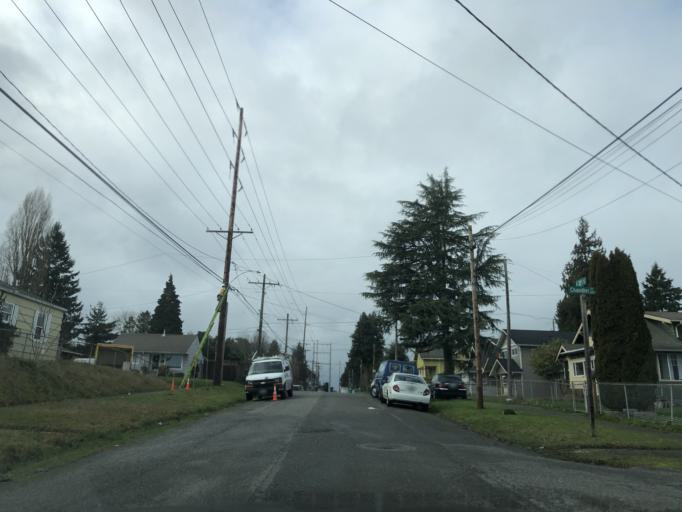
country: US
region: Washington
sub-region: Pierce County
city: Tacoma
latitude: 47.2281
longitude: -122.4558
